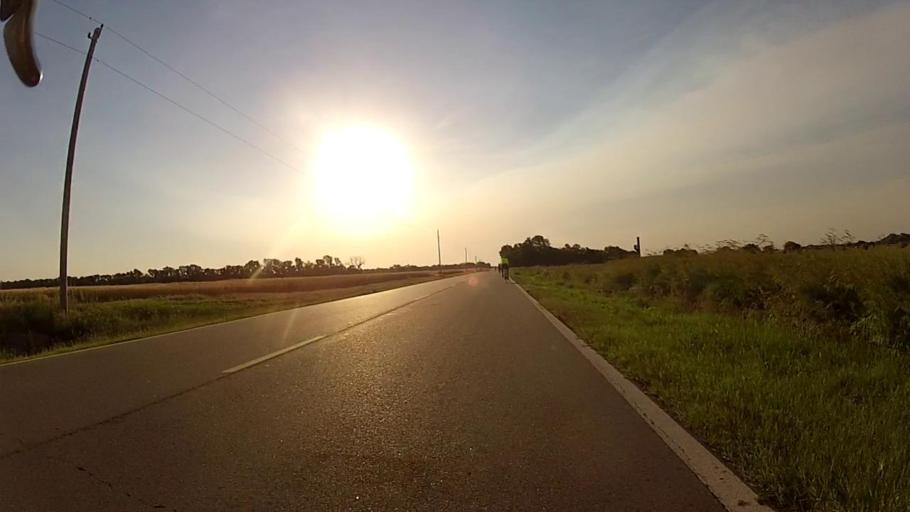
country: US
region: Kansas
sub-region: Harper County
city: Anthony
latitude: 37.1539
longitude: -97.8510
